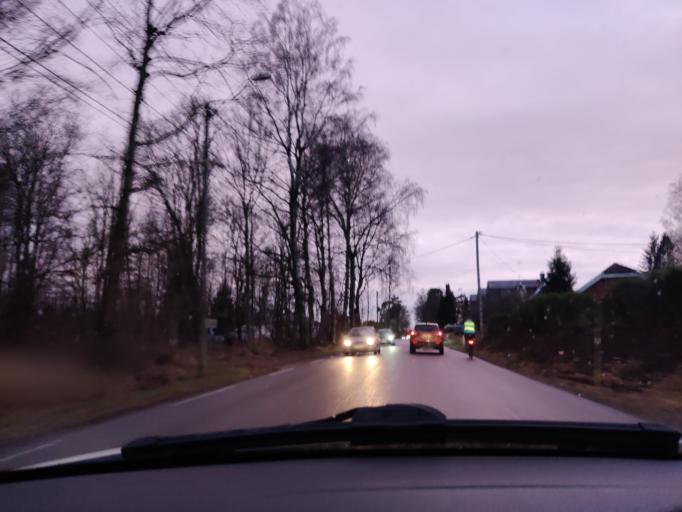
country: NO
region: Vestfold
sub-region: Tonsberg
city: Sem
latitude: 59.2684
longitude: 10.3653
